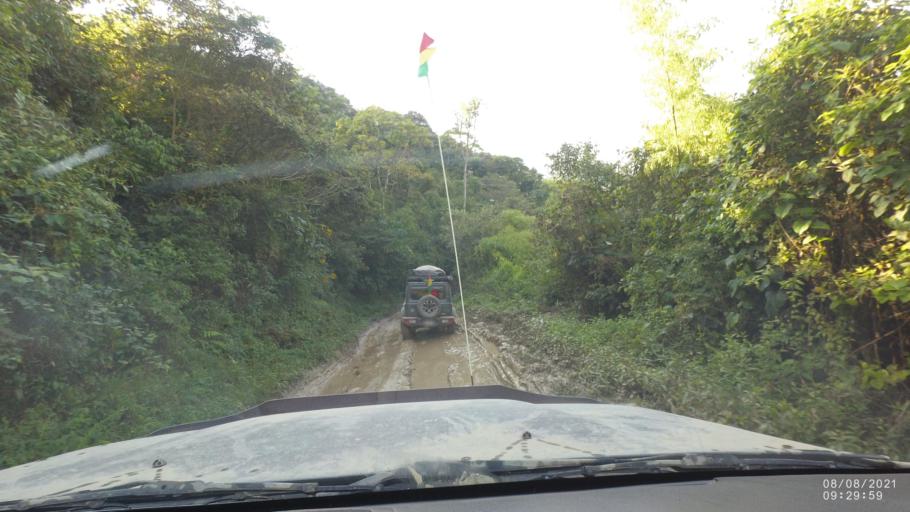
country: BO
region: La Paz
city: Quime
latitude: -16.5862
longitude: -66.7110
